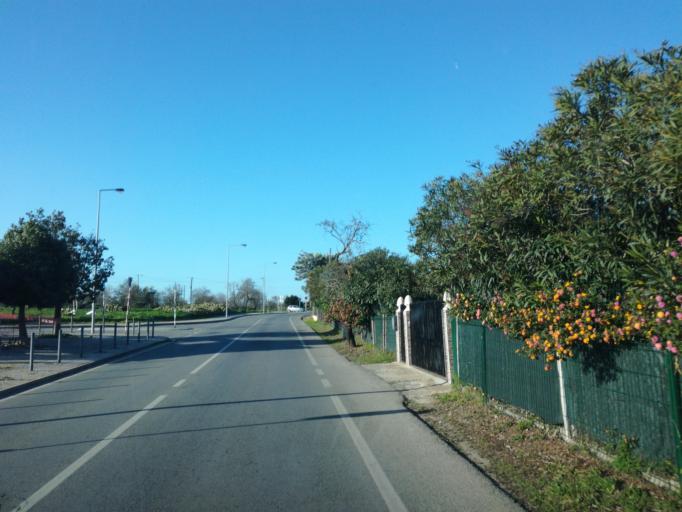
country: PT
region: Faro
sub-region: Olhao
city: Laranjeiro
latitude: 37.0543
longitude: -7.7563
